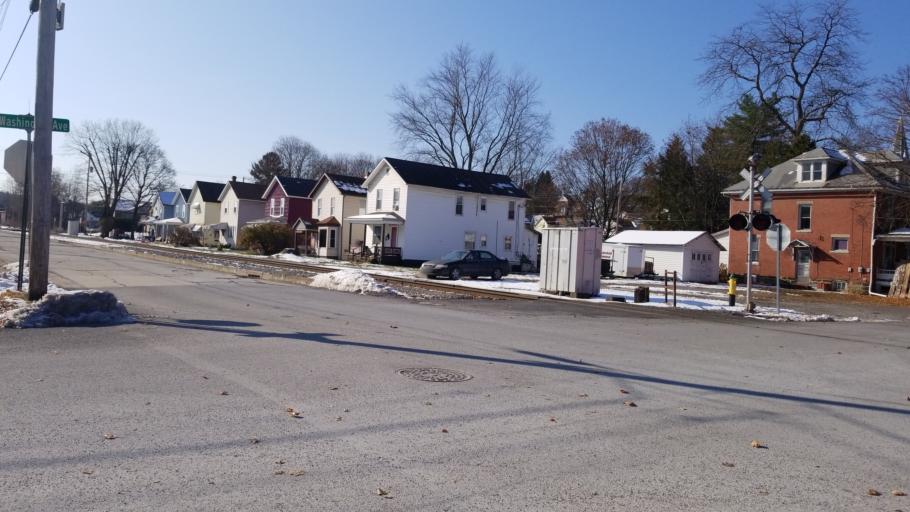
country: US
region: Pennsylvania
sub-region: Clearfield County
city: DuBois
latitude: 41.1201
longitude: -78.7663
